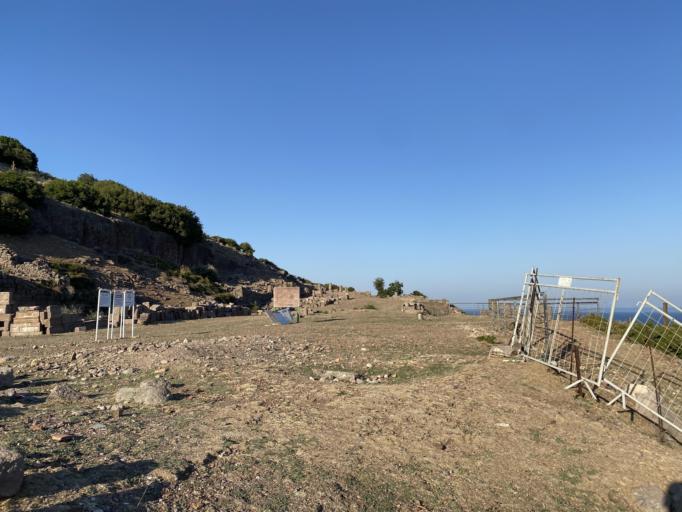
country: TR
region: Canakkale
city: Behram
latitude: 39.4889
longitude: 26.3364
